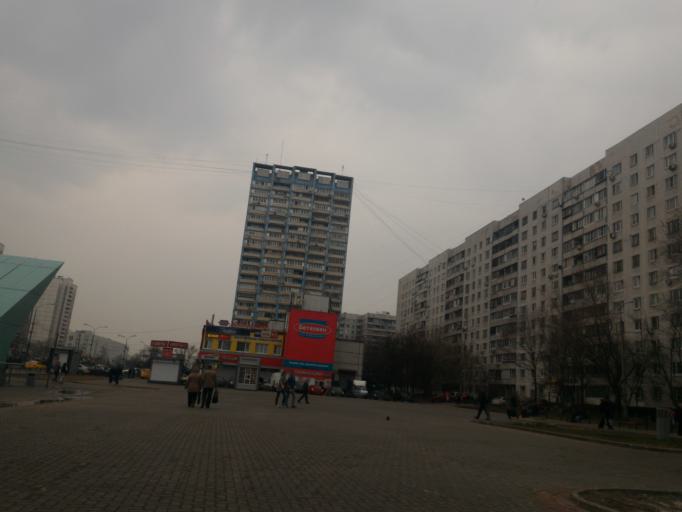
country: RU
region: Moscow
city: Strogino
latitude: 55.8046
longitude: 37.4015
